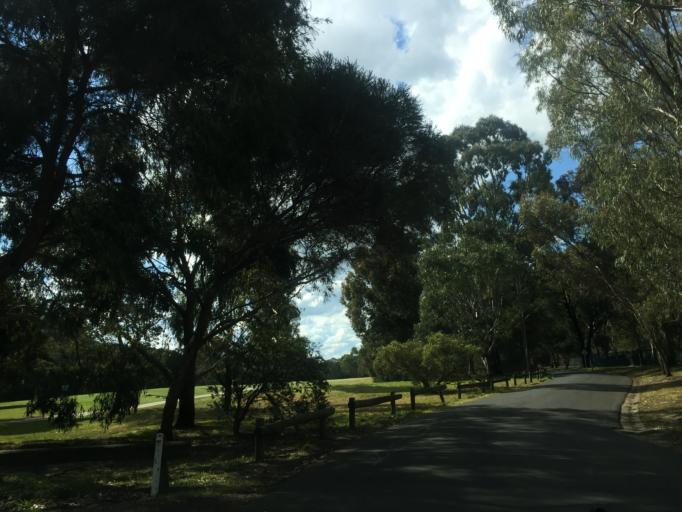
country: AU
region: Victoria
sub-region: Darebin
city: Kingsbury
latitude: -37.7091
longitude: 145.0410
